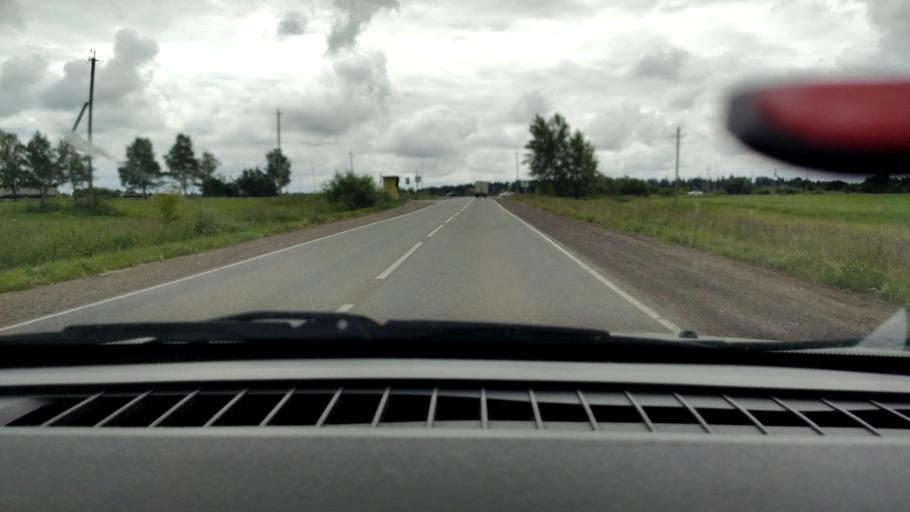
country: RU
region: Perm
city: Ust'-Kachka
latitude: 58.0703
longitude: 55.6260
